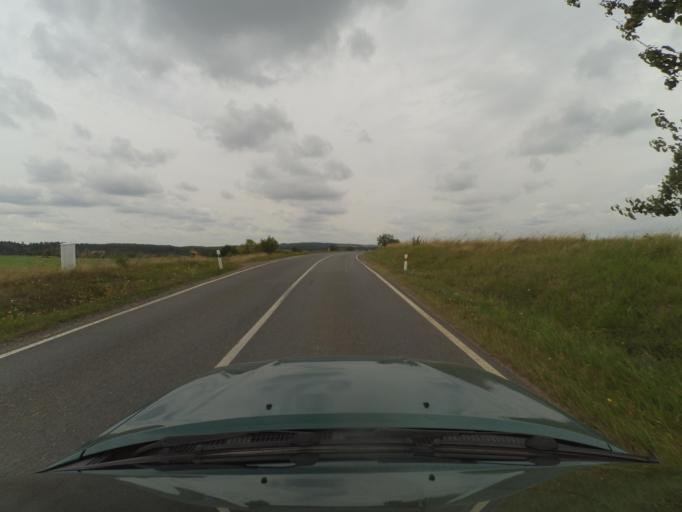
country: CZ
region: Plzensky
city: Kozlany
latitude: 50.0361
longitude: 13.6048
